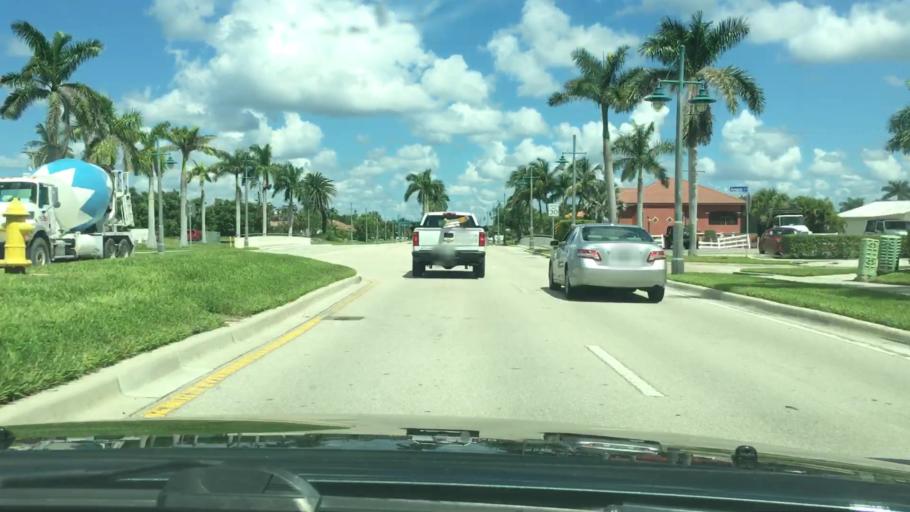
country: US
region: Florida
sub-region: Collier County
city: Marco
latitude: 25.9449
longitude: -81.7325
